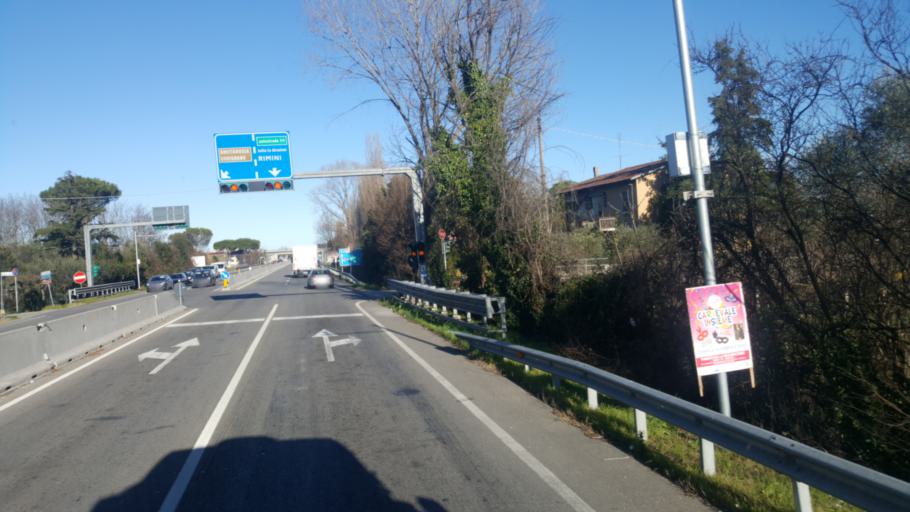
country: IT
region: Emilia-Romagna
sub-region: Provincia di Rimini
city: Rimini
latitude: 44.0345
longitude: 12.5606
